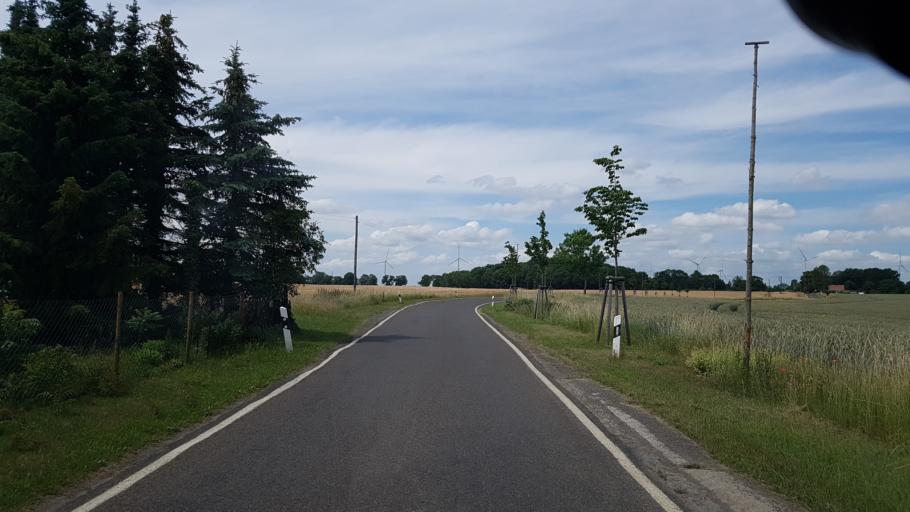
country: DE
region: Mecklenburg-Vorpommern
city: Strasburg
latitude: 53.4432
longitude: 13.7806
